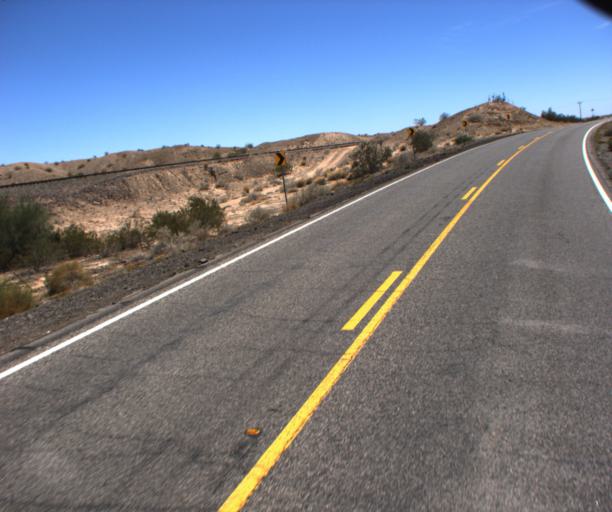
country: US
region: Arizona
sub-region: La Paz County
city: Parker
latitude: 34.0118
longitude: -114.2437
